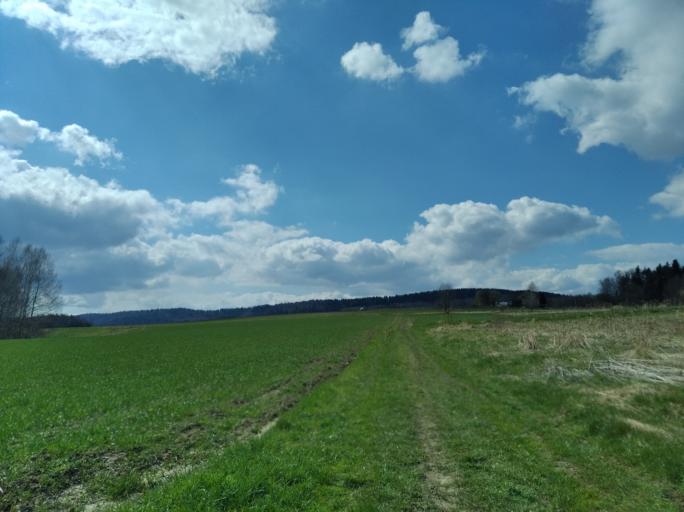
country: PL
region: Subcarpathian Voivodeship
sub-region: Powiat strzyzowski
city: Strzyzow
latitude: 49.8454
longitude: 21.7810
